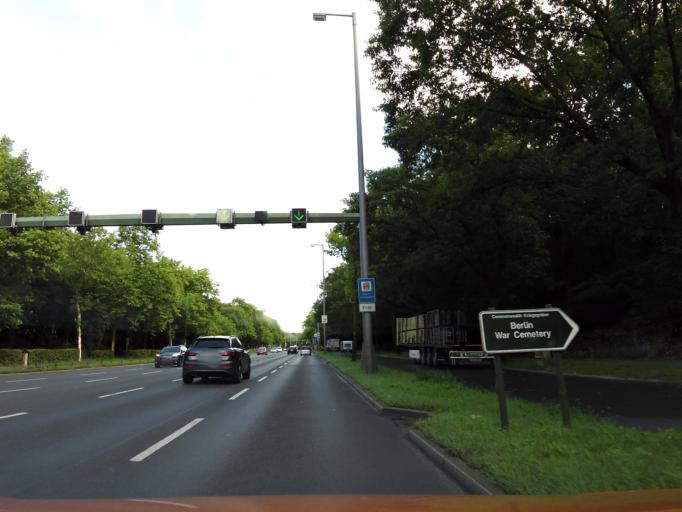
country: DE
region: Berlin
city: Haselhorst
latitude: 52.5078
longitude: 13.2227
